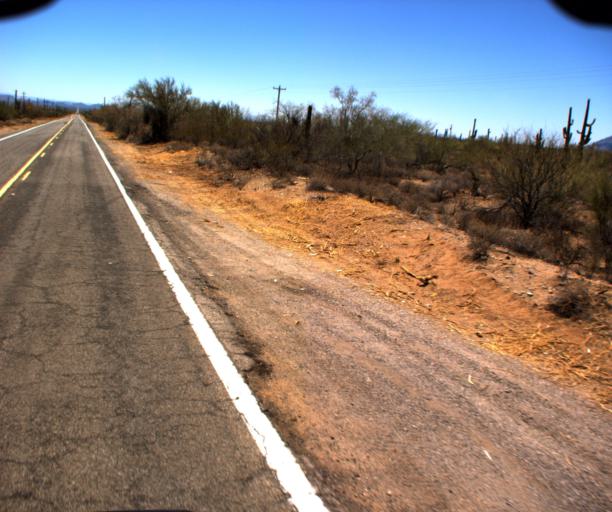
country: US
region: Arizona
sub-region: Pima County
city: Sells
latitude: 32.1396
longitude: -112.0973
